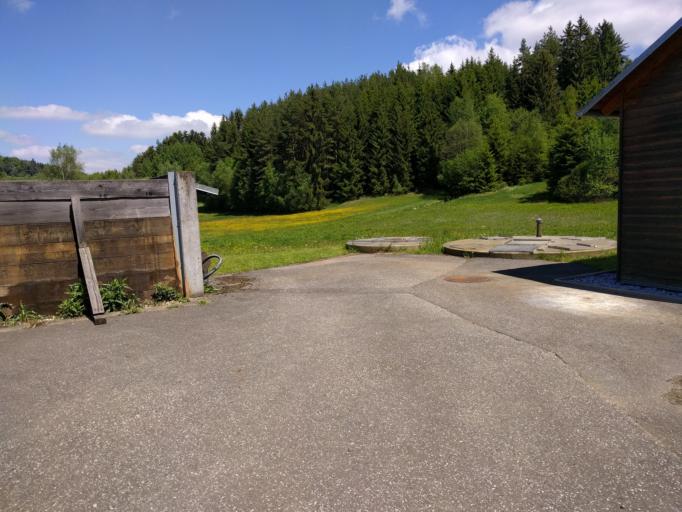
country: AT
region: Lower Austria
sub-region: Politischer Bezirk Zwettl
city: Langschlag
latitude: 48.5912
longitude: 14.9006
